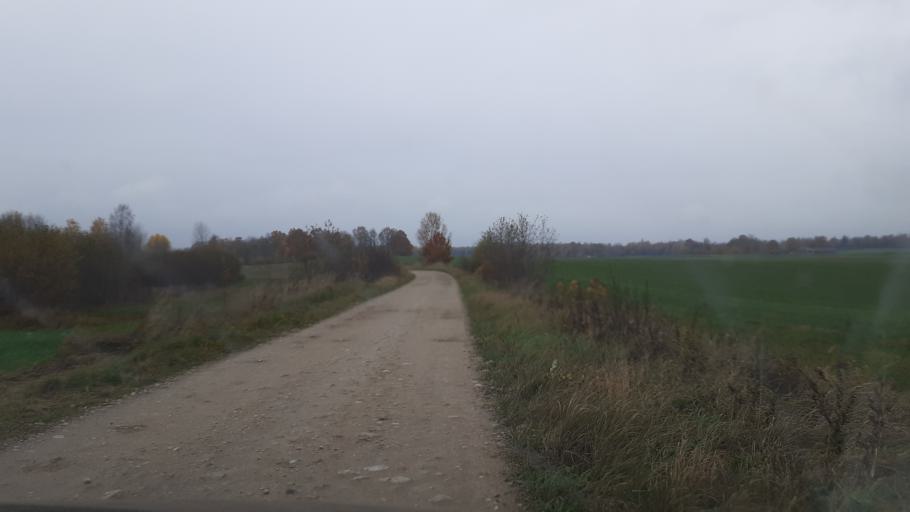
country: LV
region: Saldus Rajons
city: Saldus
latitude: 56.8669
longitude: 22.3437
